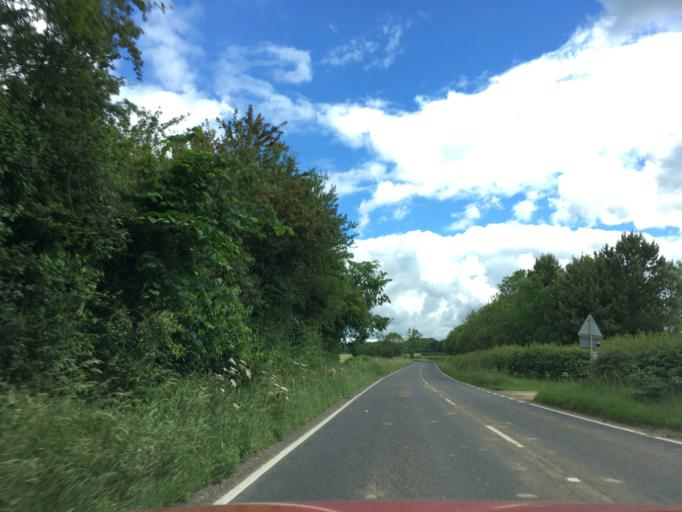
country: GB
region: England
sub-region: Oxfordshire
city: Shipton under Wychwood
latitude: 51.8790
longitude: -1.5751
